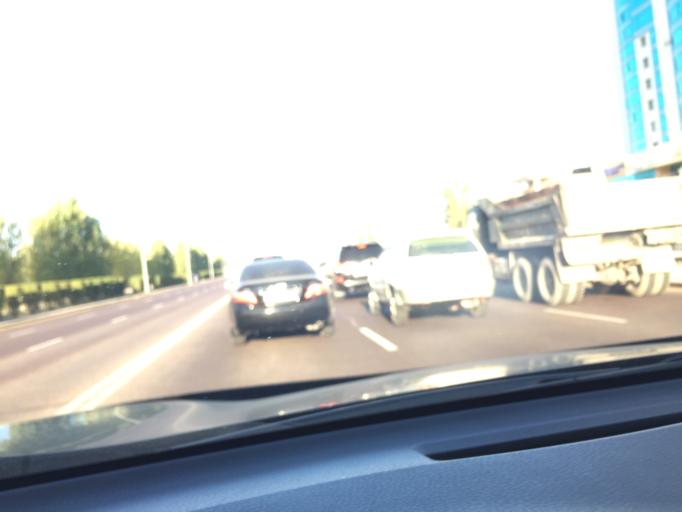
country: KZ
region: Astana Qalasy
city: Astana
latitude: 51.1354
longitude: 71.4224
